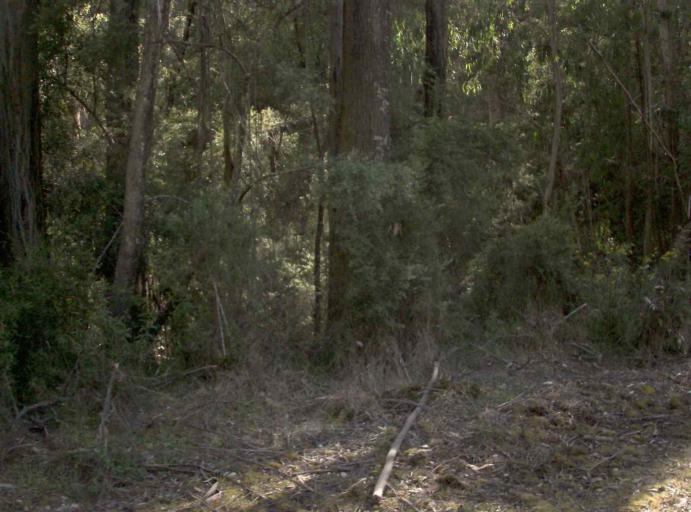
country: AU
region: Victoria
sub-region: East Gippsland
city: Lakes Entrance
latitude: -37.5021
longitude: 148.5437
